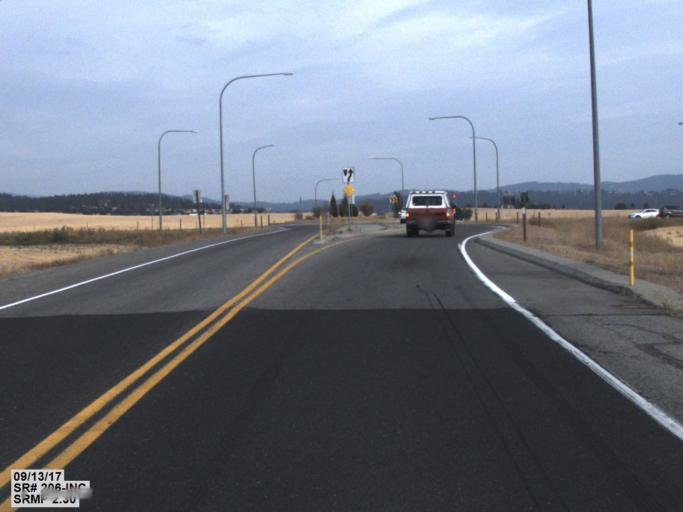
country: US
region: Washington
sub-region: Spokane County
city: Mead
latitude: 47.7876
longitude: -117.3057
